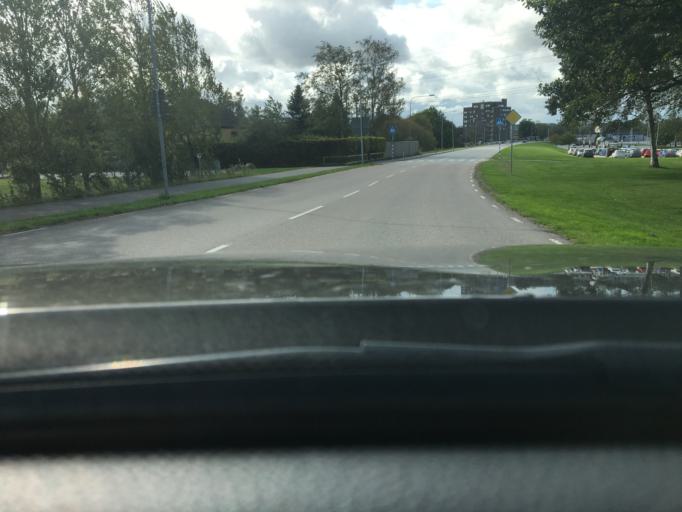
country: SE
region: Skane
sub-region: Horby Kommun
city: Hoerby
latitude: 55.8568
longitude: 13.6745
